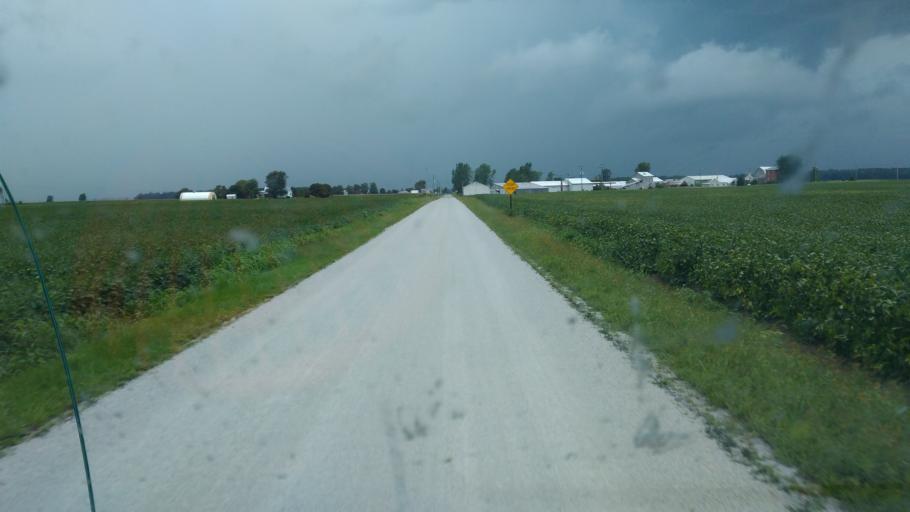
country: US
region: Ohio
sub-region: Hardin County
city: Kenton
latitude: 40.6774
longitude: -83.5145
